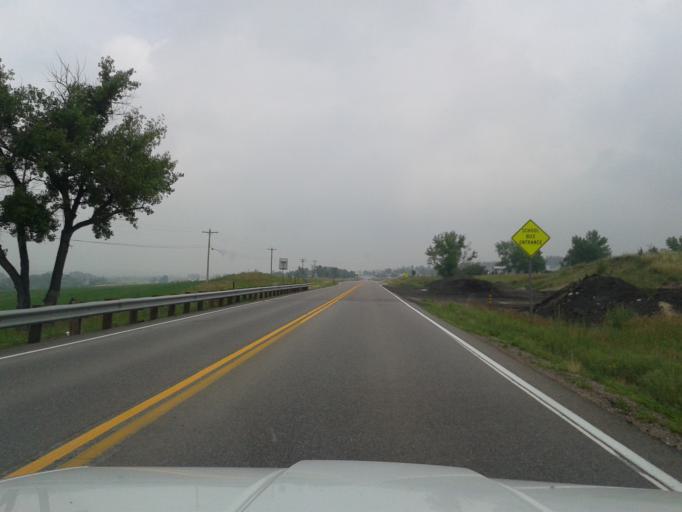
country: US
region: Colorado
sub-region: Douglas County
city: The Pinery
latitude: 39.3805
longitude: -104.7508
